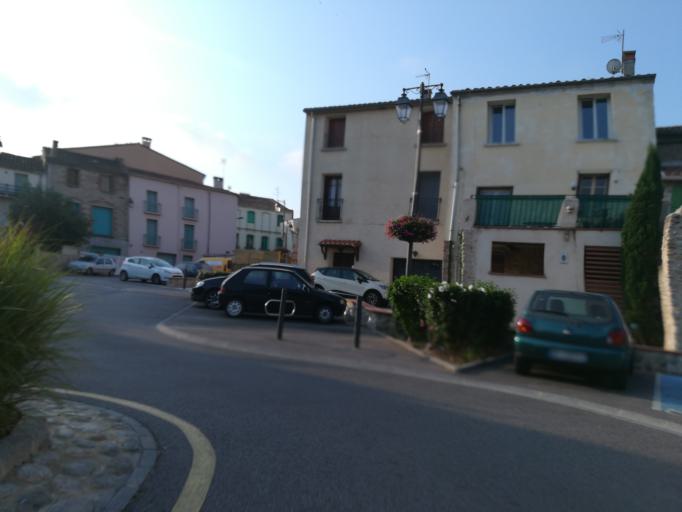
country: FR
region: Languedoc-Roussillon
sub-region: Departement des Pyrenees-Orientales
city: Maureillas-las-Illas
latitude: 42.4912
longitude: 2.8066
